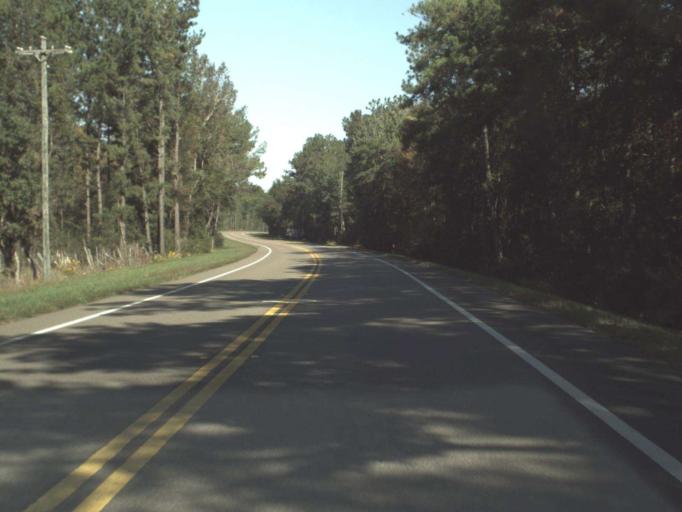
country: US
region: Florida
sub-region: Walton County
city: DeFuniak Springs
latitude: 30.6133
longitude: -85.9419
